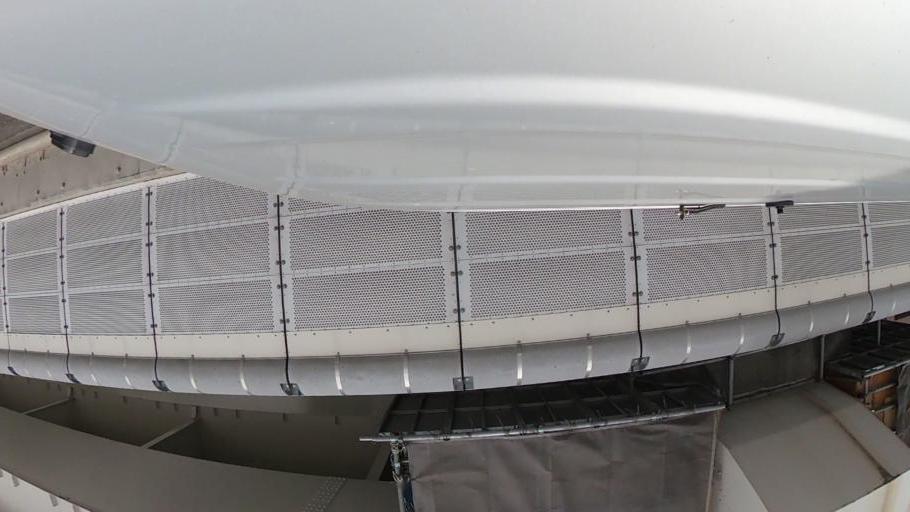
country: JP
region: Tokyo
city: Tokyo
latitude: 35.6463
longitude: 139.7567
